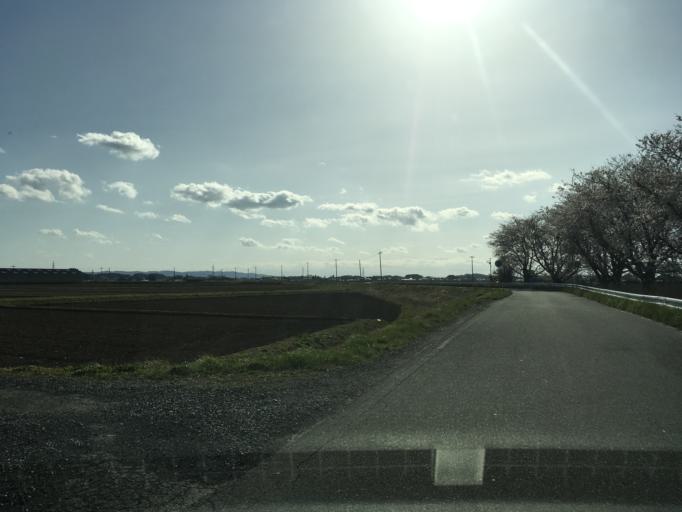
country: JP
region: Miyagi
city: Wakuya
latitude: 38.6631
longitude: 141.2420
